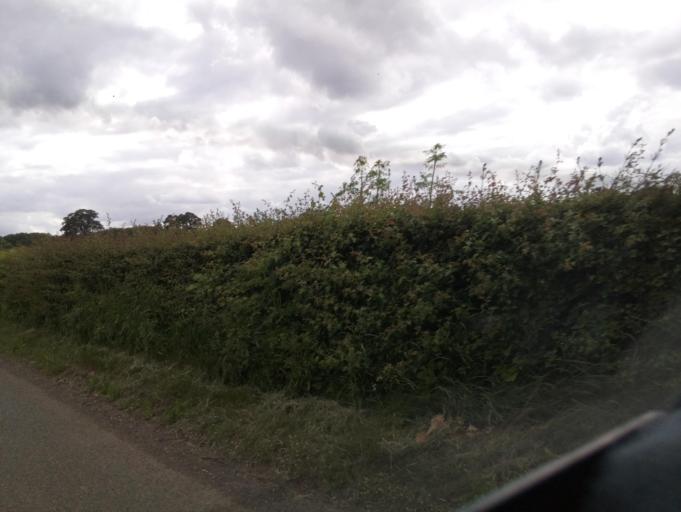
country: GB
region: England
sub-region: Herefordshire
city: Yatton
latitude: 51.9910
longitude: -2.5048
